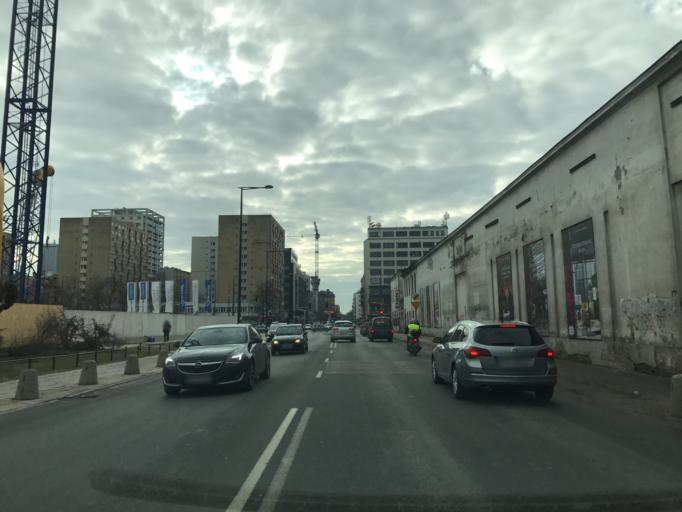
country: PL
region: Masovian Voivodeship
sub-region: Warszawa
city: Wola
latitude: 52.2329
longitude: 20.9918
